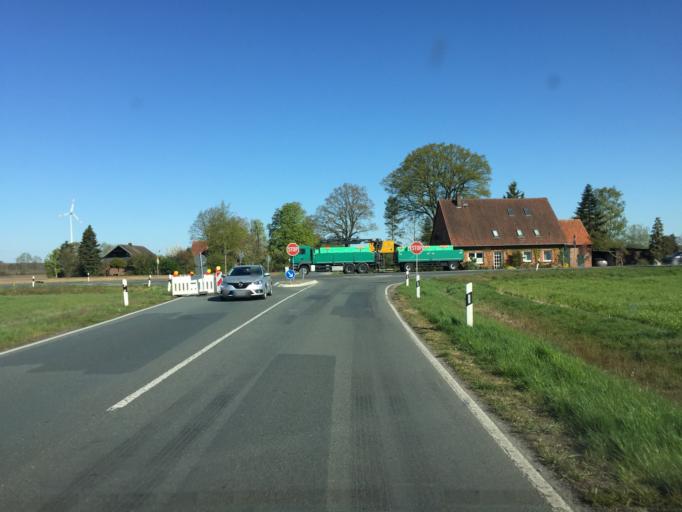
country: DE
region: Lower Saxony
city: Varrel
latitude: 52.6455
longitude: 8.7320
